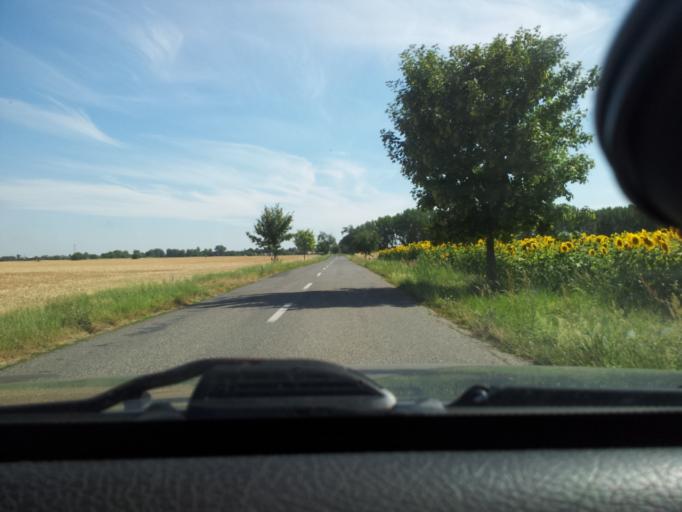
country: SK
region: Nitriansky
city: Tlmace
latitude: 48.2608
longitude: 18.5354
